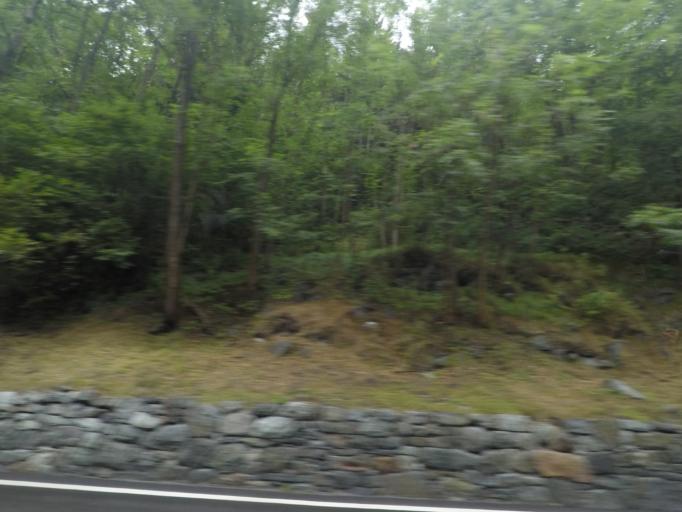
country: IT
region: Aosta Valley
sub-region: Valle d'Aosta
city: Chamois
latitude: 45.8378
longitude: 7.6034
